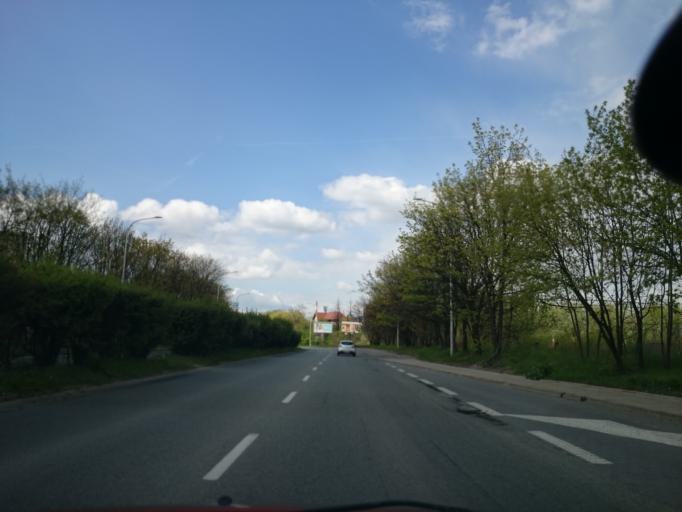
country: PL
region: Opole Voivodeship
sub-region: Powiat opolski
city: Opole
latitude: 50.6714
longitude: 17.9392
